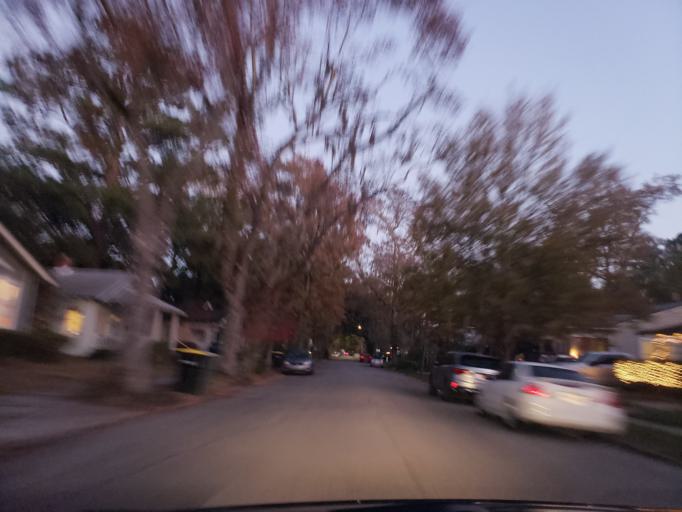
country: US
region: Georgia
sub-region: Chatham County
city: Thunderbolt
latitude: 32.0436
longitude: -81.0840
